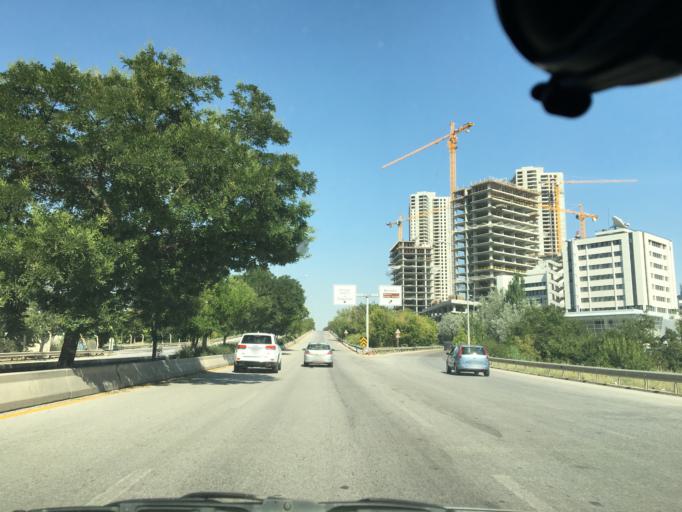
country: TR
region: Ankara
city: Ankara
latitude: 39.9183
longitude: 32.7854
